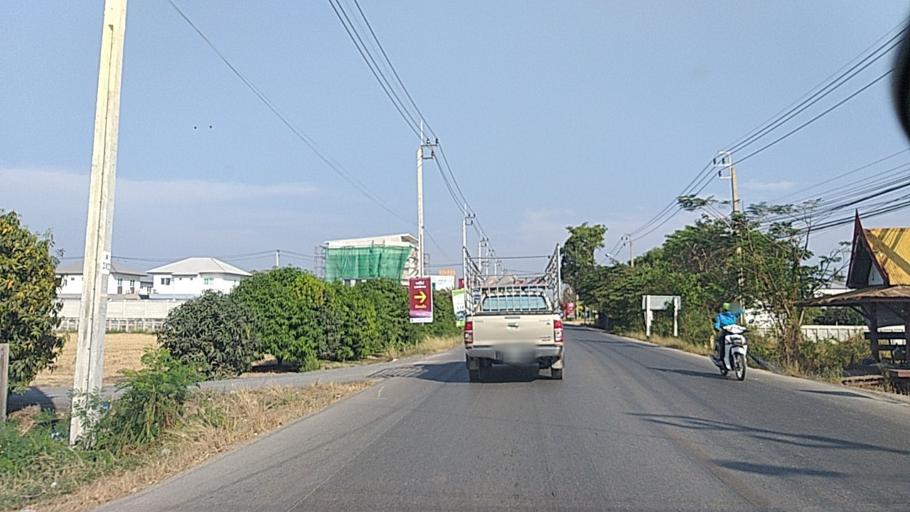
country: TH
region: Nonthaburi
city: Bang Bua Thong
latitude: 13.9352
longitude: 100.3702
